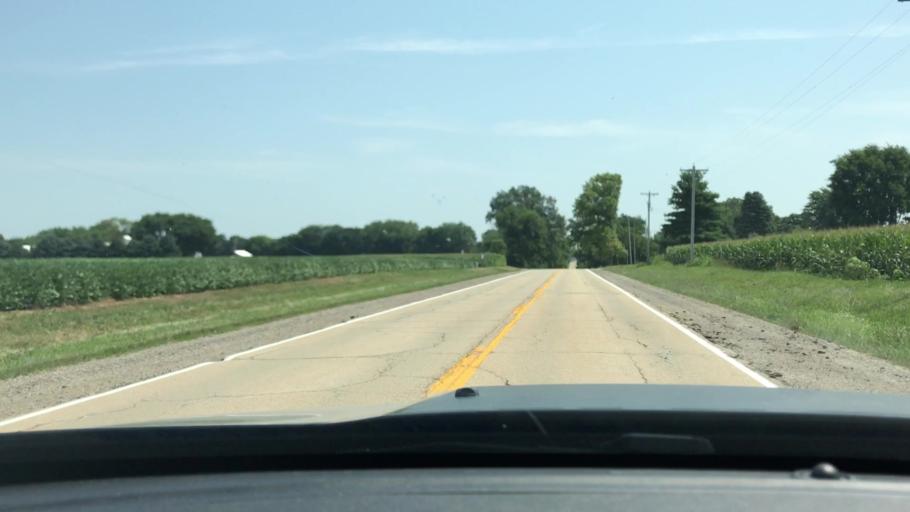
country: US
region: Illinois
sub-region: LaSalle County
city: Sheridan
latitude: 41.4852
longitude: -88.7792
